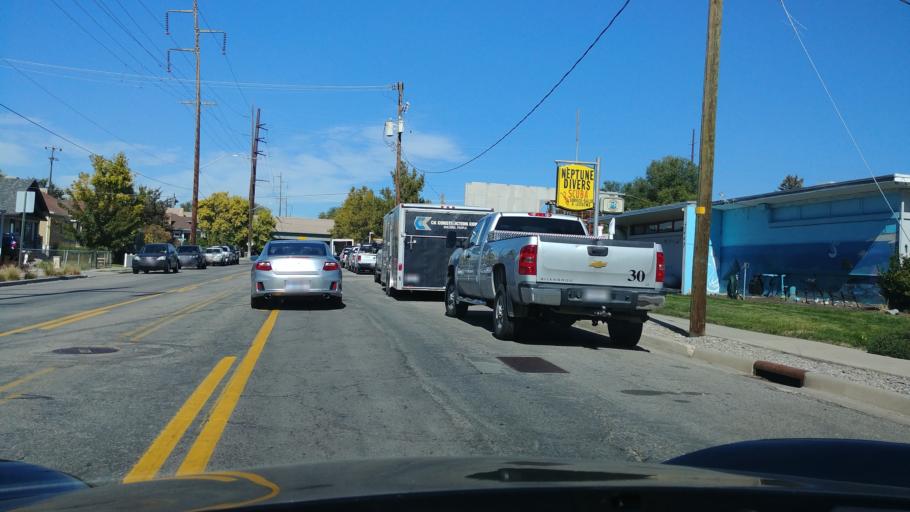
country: US
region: Utah
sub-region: Salt Lake County
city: South Salt Lake
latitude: 40.7173
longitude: -111.8654
